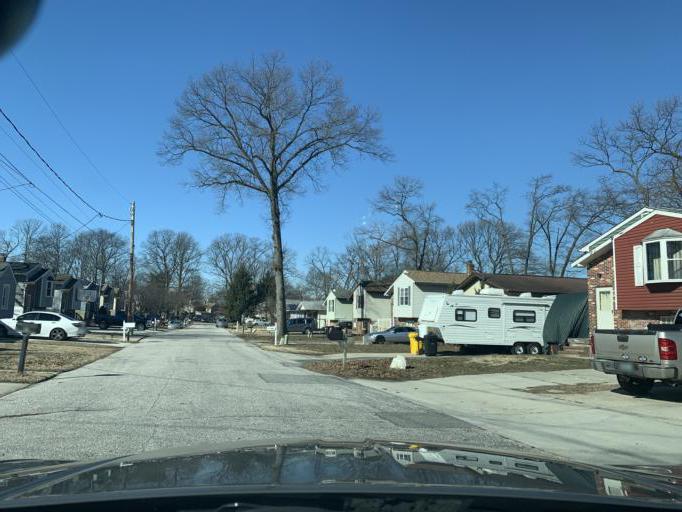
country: US
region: Maryland
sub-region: Anne Arundel County
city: Glen Burnie
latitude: 39.1596
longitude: -76.6347
